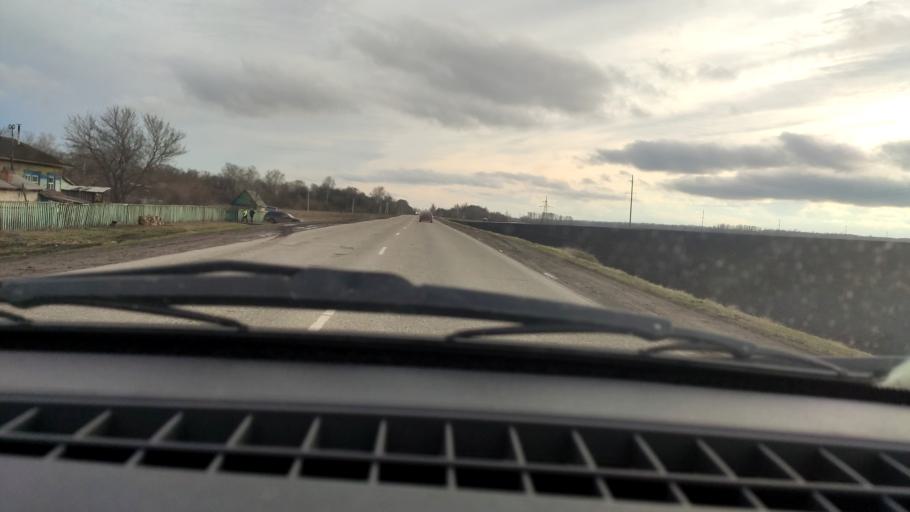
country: RU
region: Bashkortostan
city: Chishmy
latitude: 54.5498
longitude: 55.3306
